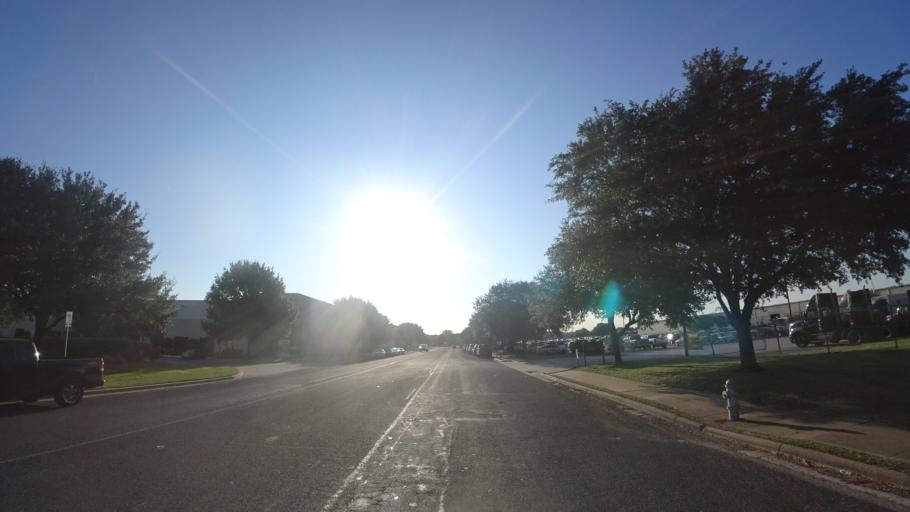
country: US
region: Texas
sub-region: Travis County
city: Manor
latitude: 30.3375
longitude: -97.6606
